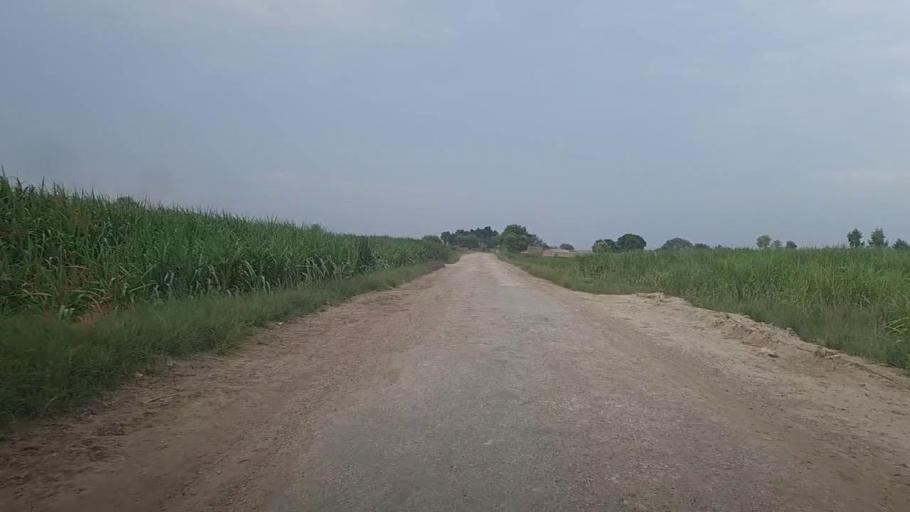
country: PK
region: Sindh
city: Kashmor
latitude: 28.3740
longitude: 69.7834
